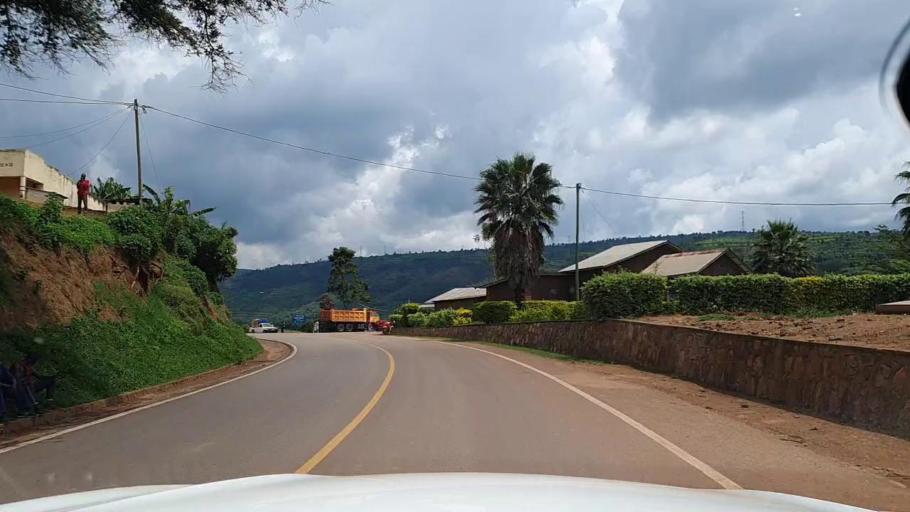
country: RW
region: Kigali
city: Kigali
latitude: -1.8080
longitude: 30.1252
